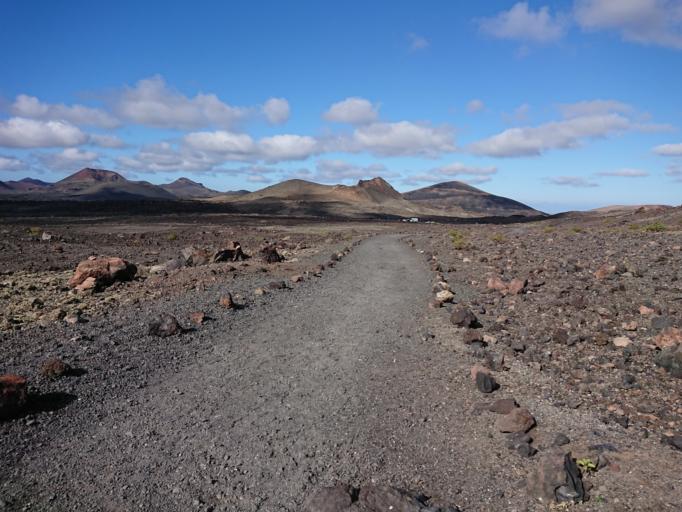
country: ES
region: Canary Islands
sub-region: Provincia de Las Palmas
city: Tias
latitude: 29.0030
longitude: -13.6812
